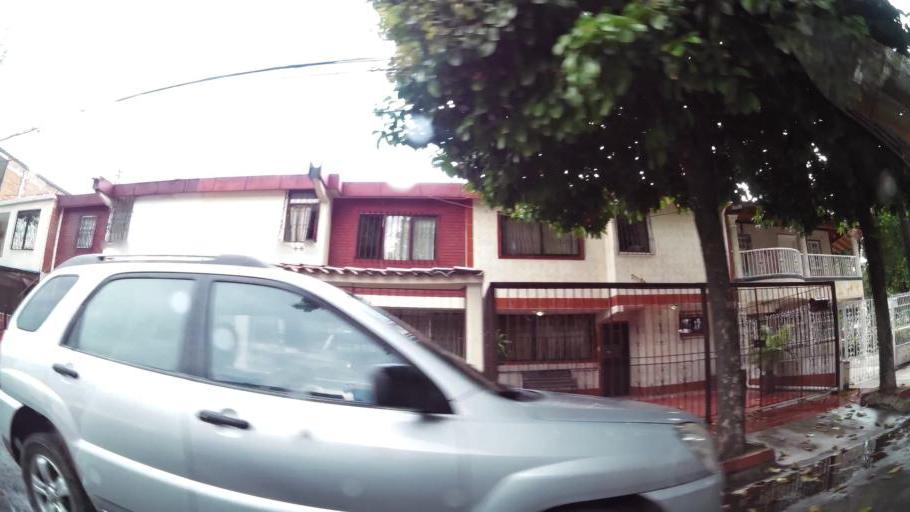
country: CO
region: Valle del Cauca
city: Cali
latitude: 3.4802
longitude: -76.5125
